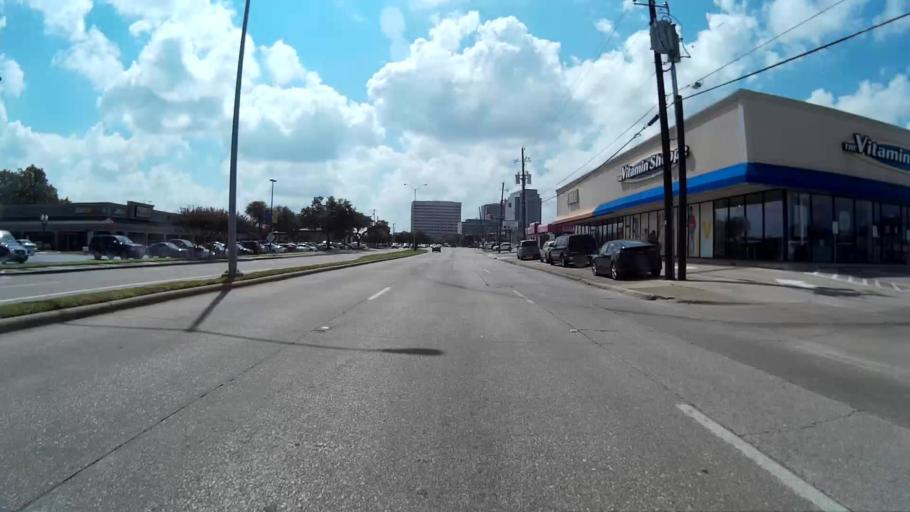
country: US
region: Texas
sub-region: Dallas County
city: Highland Park
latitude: 32.8530
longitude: -96.7696
